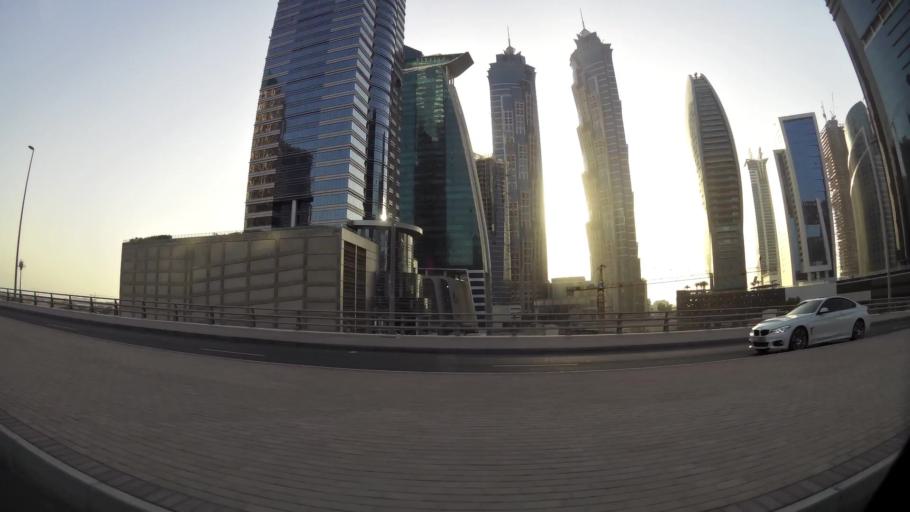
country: AE
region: Dubai
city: Dubai
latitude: 25.1841
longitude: 55.2621
